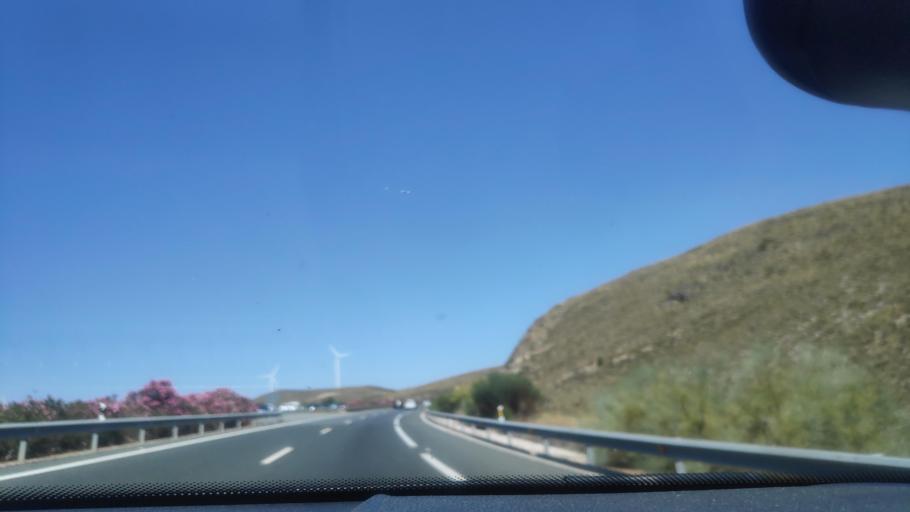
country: ES
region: Andalusia
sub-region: Provincia de Granada
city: Padul
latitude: 36.9919
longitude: -3.6246
